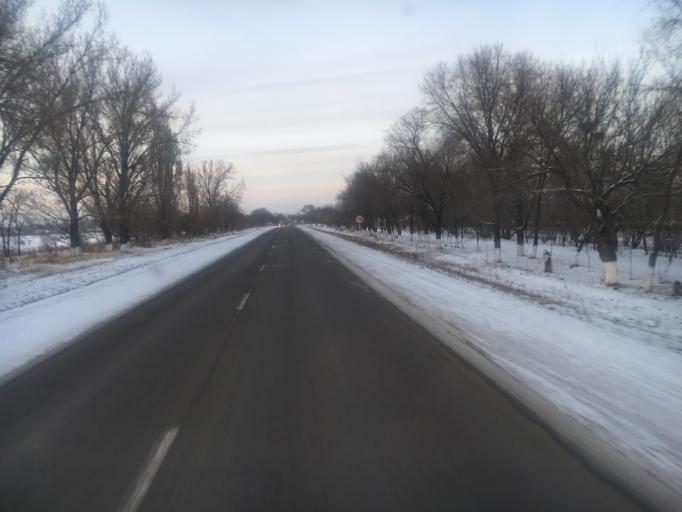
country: KZ
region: Almaty Oblysy
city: Burunday
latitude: 43.3611
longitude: 76.6435
